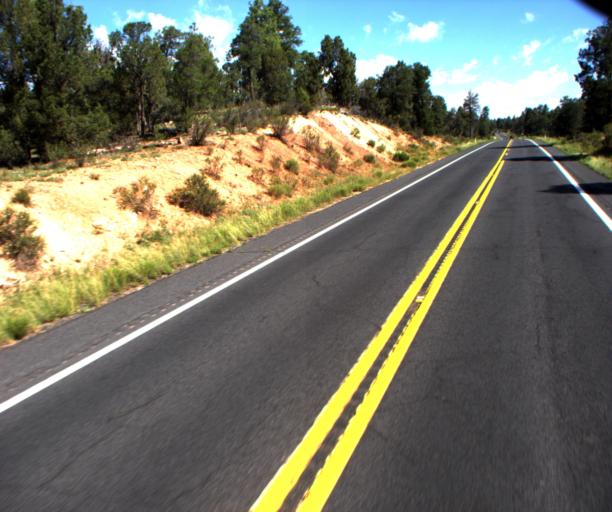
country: US
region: Arizona
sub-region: Coconino County
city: Grand Canyon Village
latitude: 35.8948
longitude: -112.1302
